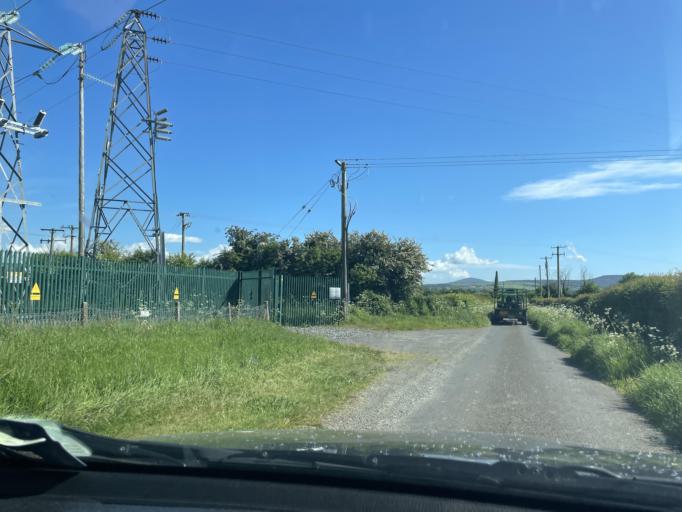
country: IE
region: Leinster
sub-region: County Carlow
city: Bagenalstown
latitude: 52.6344
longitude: -7.0156
